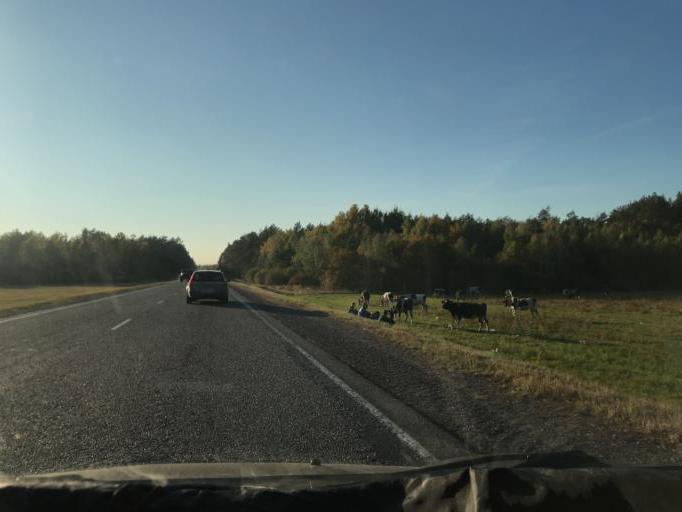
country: BY
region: Gomel
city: Zhytkavichy
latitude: 52.2727
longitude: 28.0199
